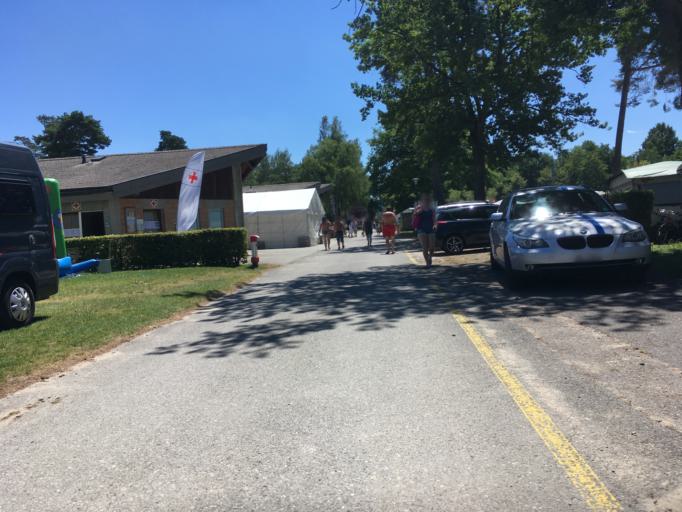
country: CH
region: Vaud
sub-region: Broye-Vully District
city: Avenches
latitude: 46.9053
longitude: 7.0488
